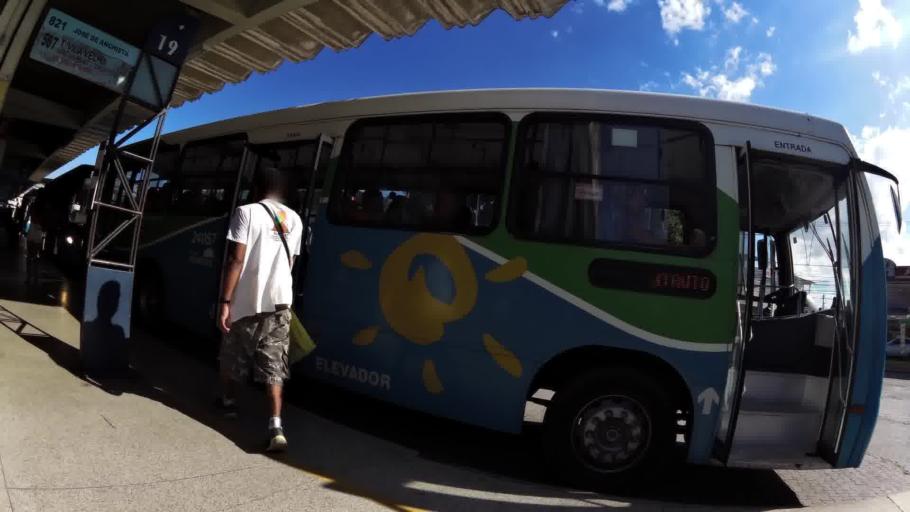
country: BR
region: Espirito Santo
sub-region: Vila Velha
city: Vila Velha
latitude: -20.2302
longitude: -40.2703
